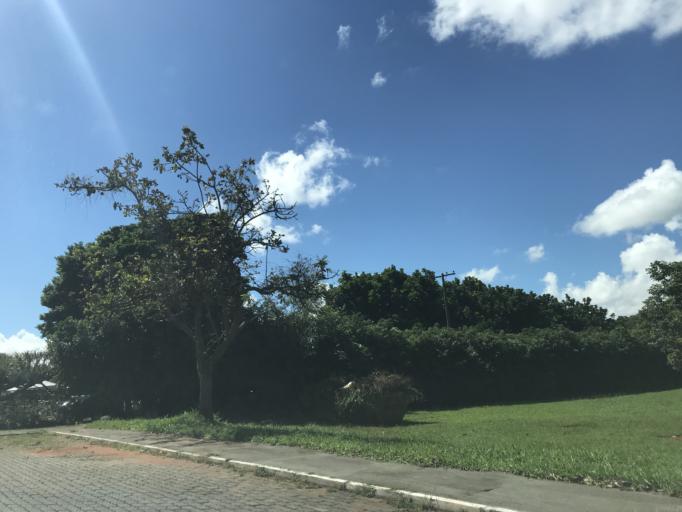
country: BR
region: Federal District
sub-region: Brasilia
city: Brasilia
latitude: -15.8232
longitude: -47.8958
